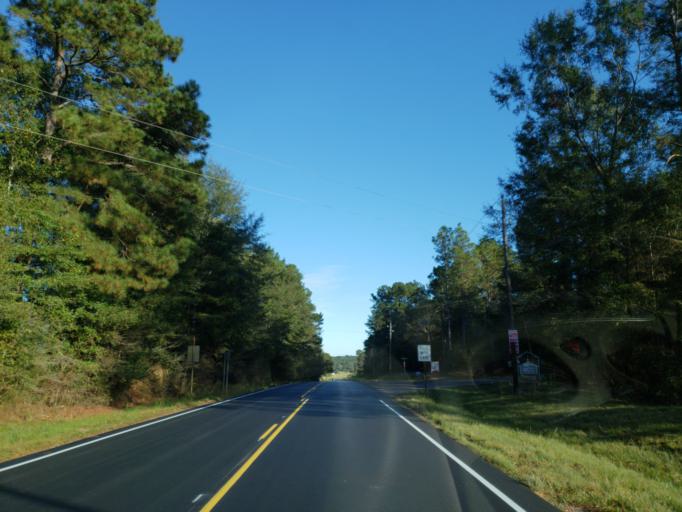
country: US
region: Mississippi
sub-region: Perry County
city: Richton
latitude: 31.3697
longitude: -88.8203
